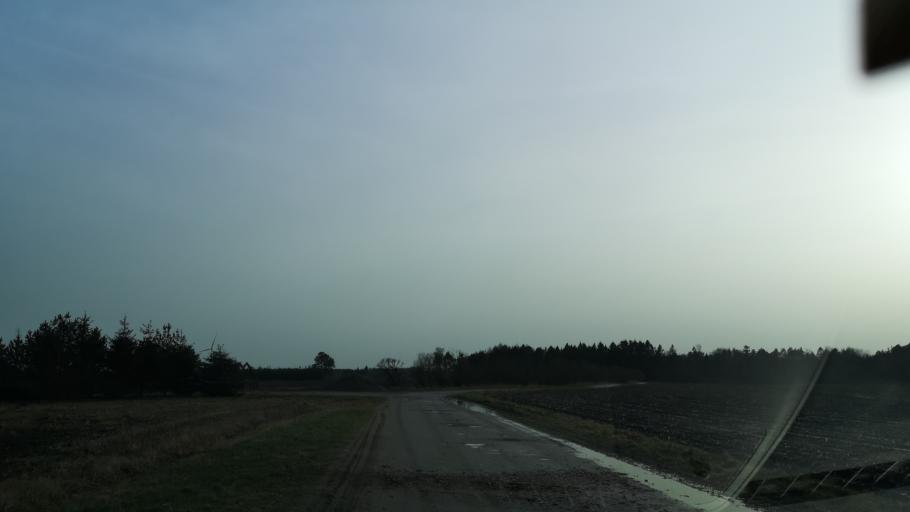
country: DK
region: Central Jutland
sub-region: Ikast-Brande Kommune
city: Brande
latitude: 56.0022
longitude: 9.1152
